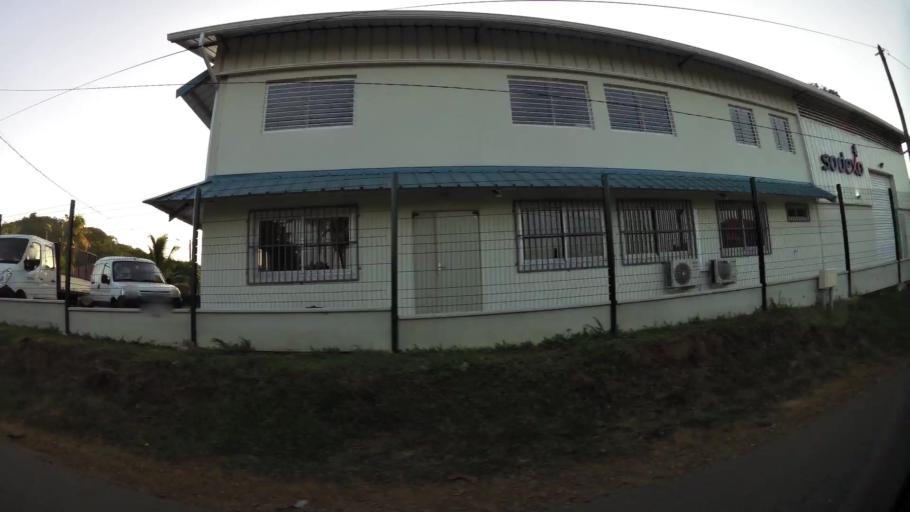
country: GF
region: Guyane
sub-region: Guyane
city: Cayenne
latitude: 4.9259
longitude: -52.3037
